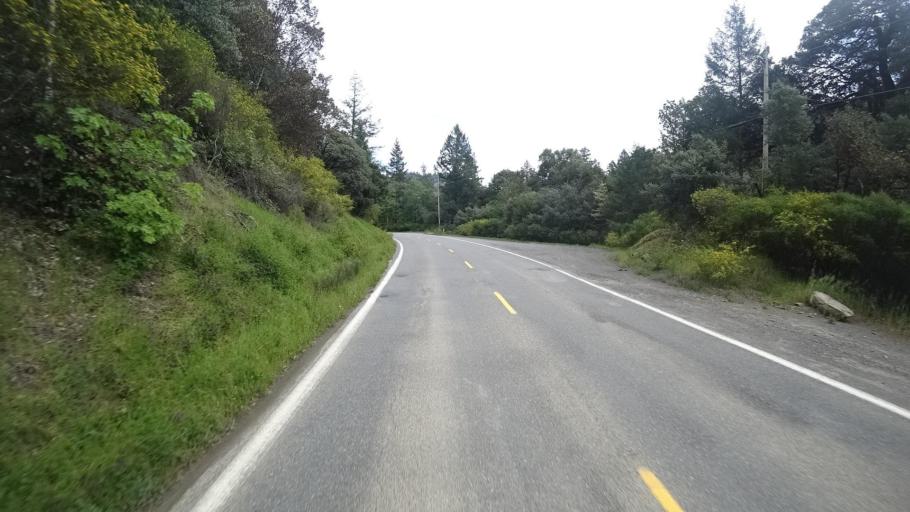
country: US
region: California
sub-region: Humboldt County
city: Redway
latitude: 40.1184
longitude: -123.8843
